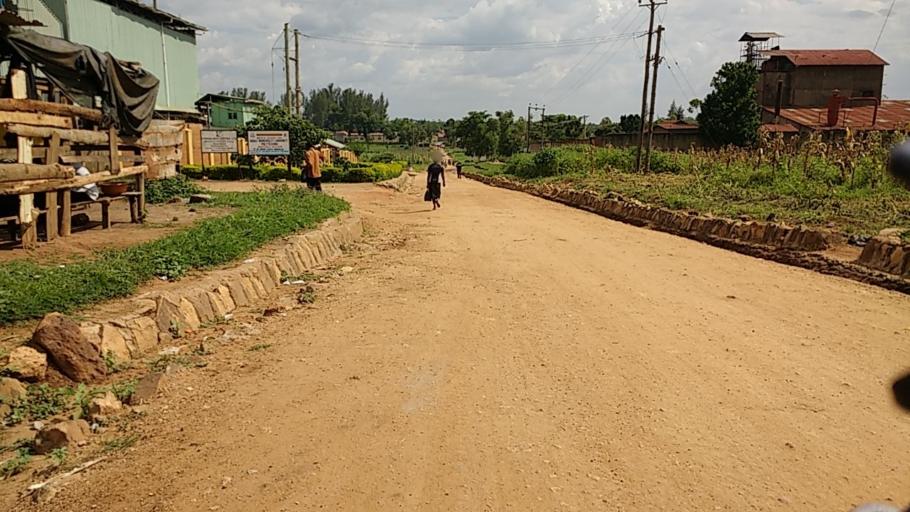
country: UG
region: Eastern Region
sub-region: Mbale District
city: Mbale
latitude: 1.0755
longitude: 34.1594
